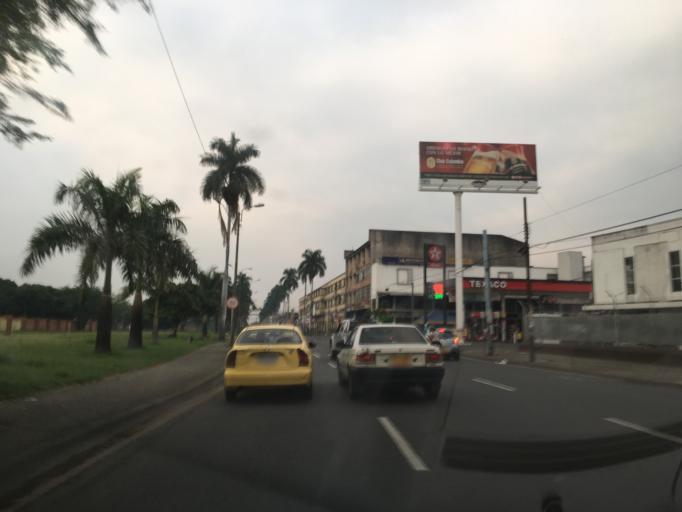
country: CO
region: Valle del Cauca
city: Cali
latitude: 3.4588
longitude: -76.5208
